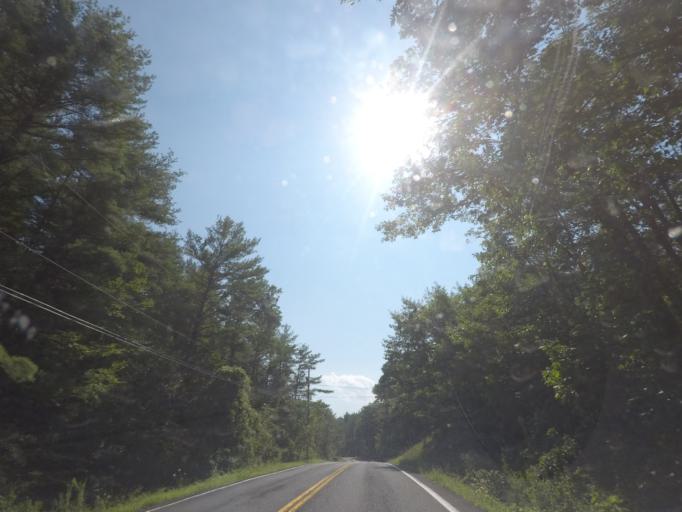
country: US
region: New York
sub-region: Rensselaer County
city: Hoosick Falls
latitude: 42.8325
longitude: -73.4748
